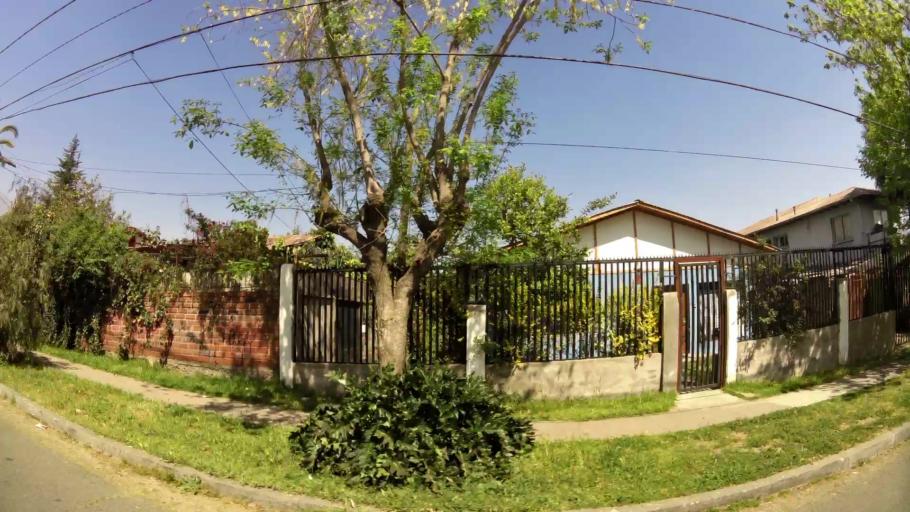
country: CL
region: Santiago Metropolitan
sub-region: Provincia de Santiago
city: Villa Presidente Frei, Nunoa, Santiago, Chile
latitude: -33.4641
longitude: -70.5391
